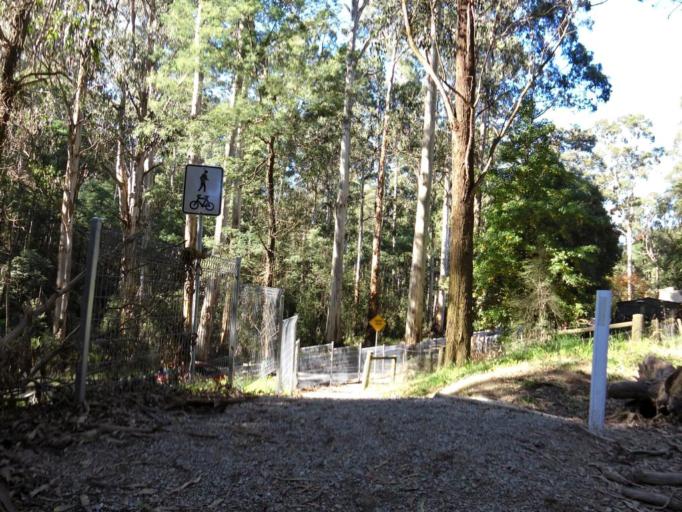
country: AU
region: Victoria
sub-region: Cardinia
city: Cockatoo
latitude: -37.9432
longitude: 145.4947
